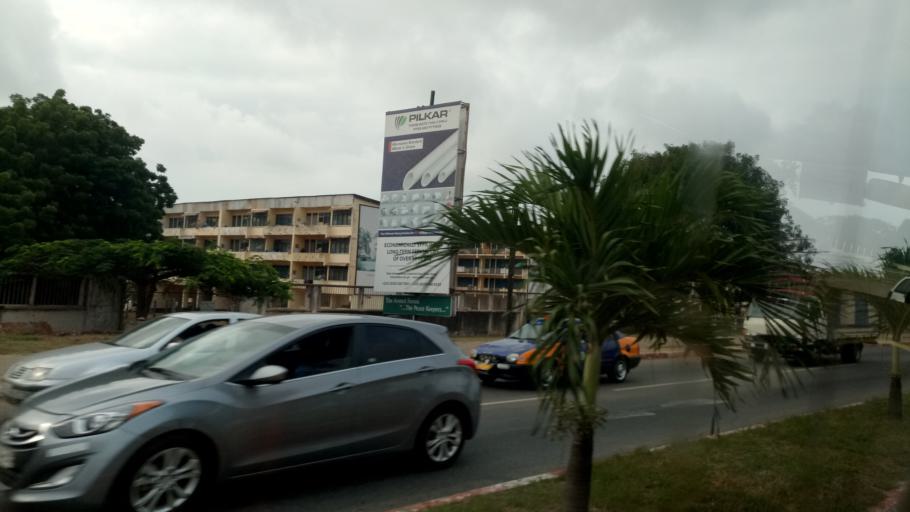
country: GH
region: Greater Accra
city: Accra
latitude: 5.5787
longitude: -0.1871
